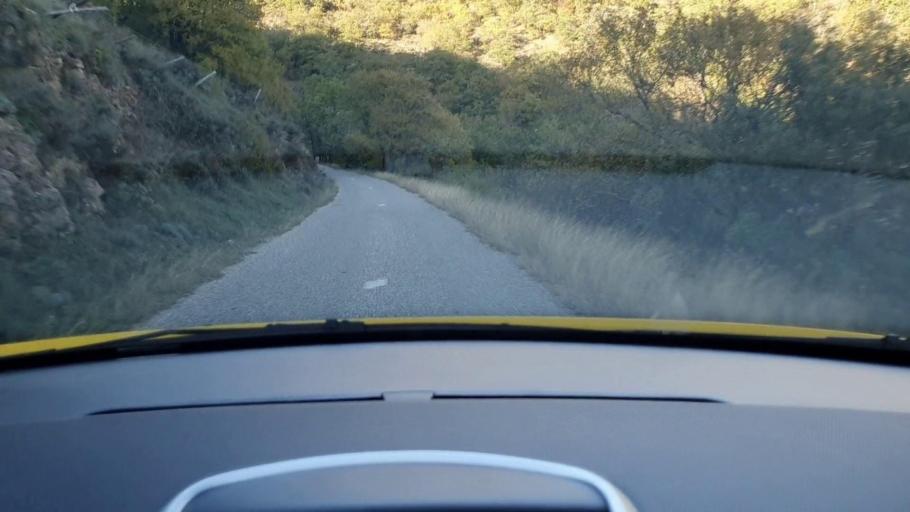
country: FR
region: Languedoc-Roussillon
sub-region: Departement du Gard
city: Sumene
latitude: 43.9786
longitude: 3.7628
